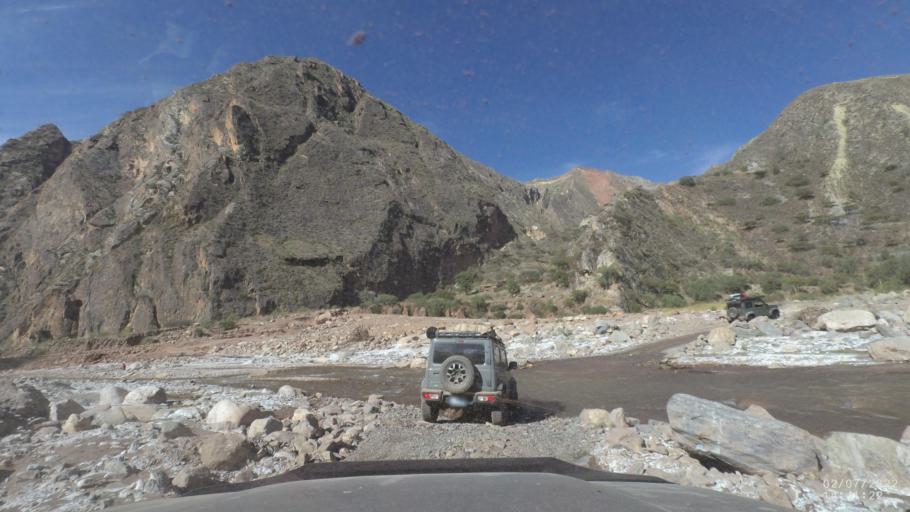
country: BO
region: Cochabamba
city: Irpa Irpa
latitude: -17.8497
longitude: -66.4206
